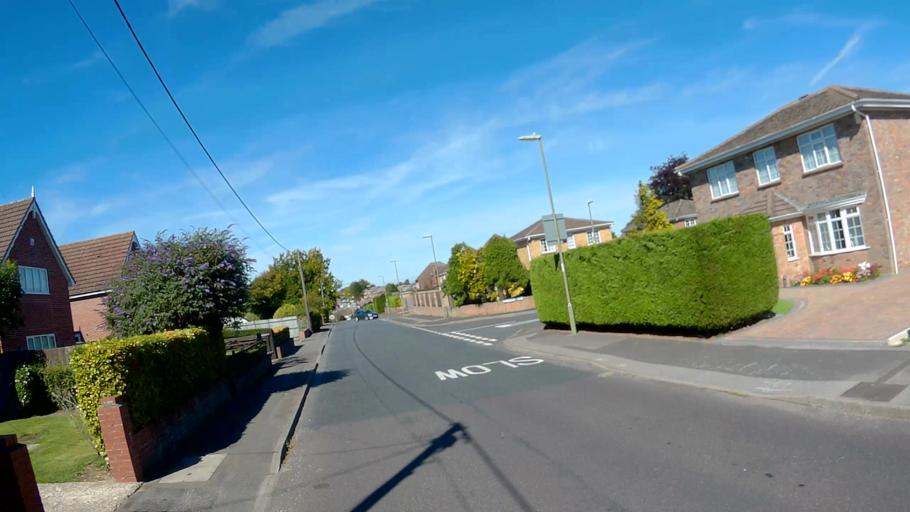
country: GB
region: England
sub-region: Hampshire
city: Basingstoke
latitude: 51.2472
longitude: -1.1378
